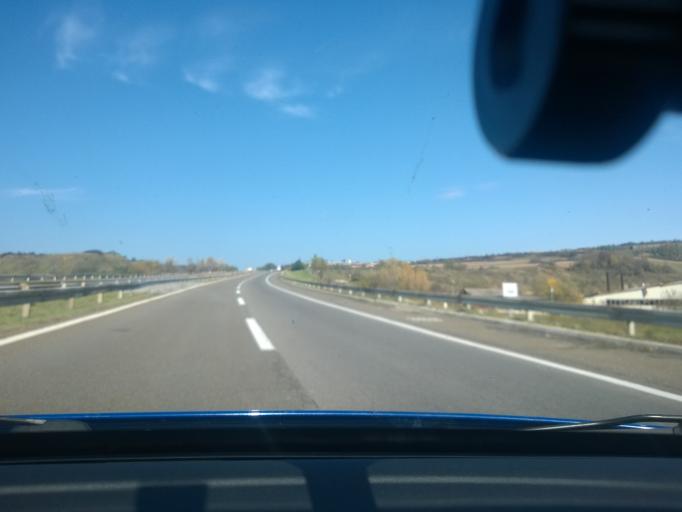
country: RS
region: Central Serbia
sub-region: Nisavski Okrug
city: Razanj
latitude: 43.6602
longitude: 21.5505
